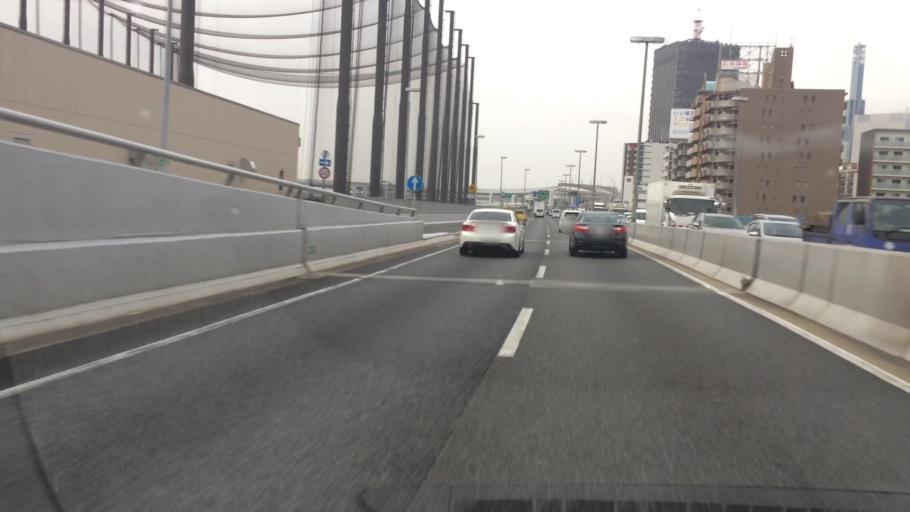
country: JP
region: Hyogo
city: Kobe
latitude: 34.6922
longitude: 135.2029
